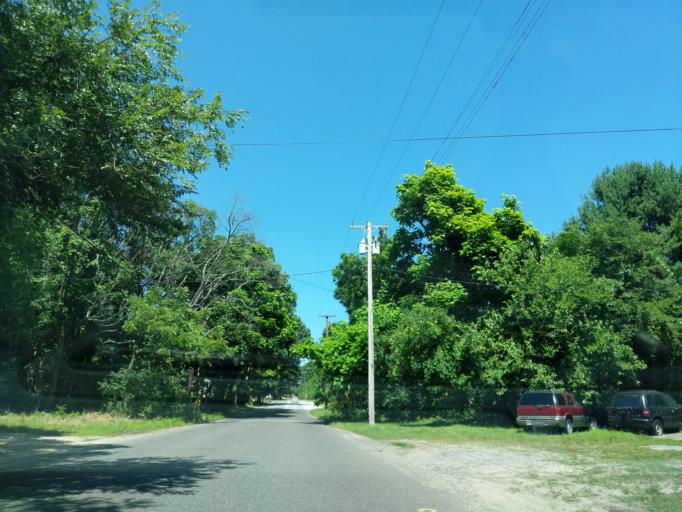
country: US
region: New Jersey
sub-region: Gloucester County
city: Wenonah
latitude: 39.7966
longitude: -75.1408
